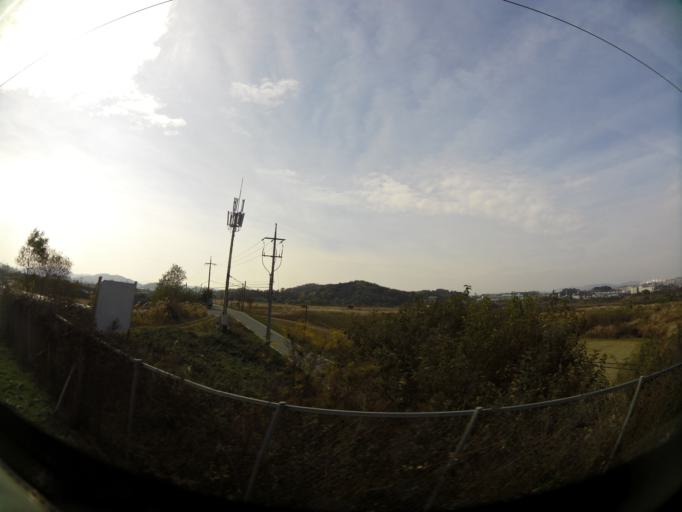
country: KR
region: Daejeon
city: Songgang-dong
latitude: 36.5799
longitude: 127.3090
